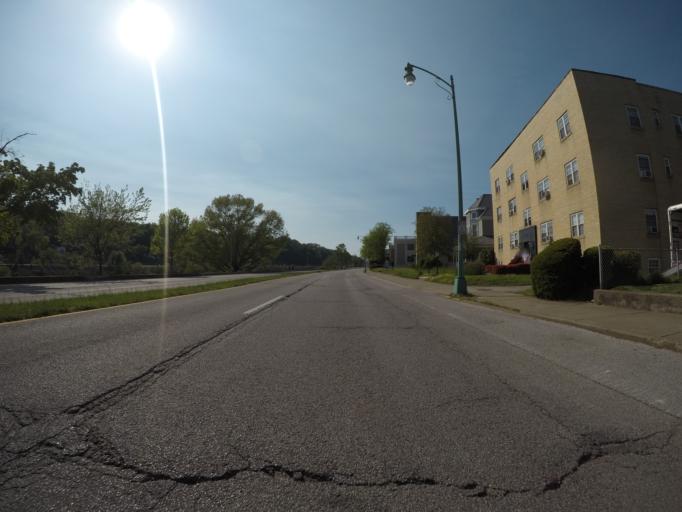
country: US
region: West Virginia
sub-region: Kanawha County
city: Charleston
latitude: 38.3407
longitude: -81.6266
